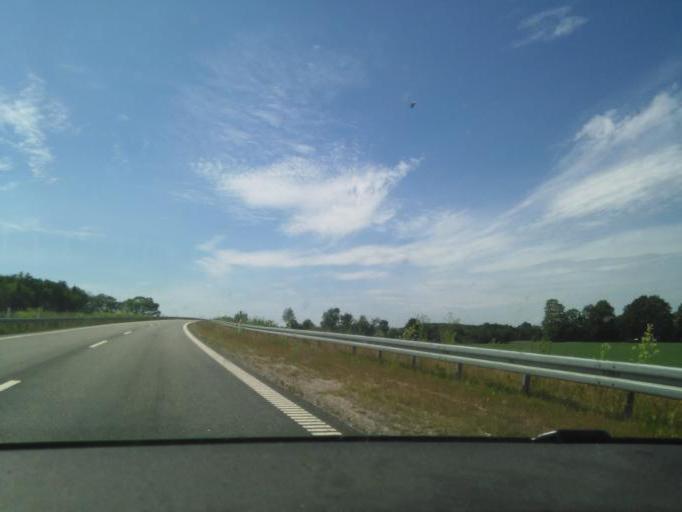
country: DK
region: Zealand
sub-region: Holbaek Kommune
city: Vipperod
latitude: 55.6446
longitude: 11.7523
